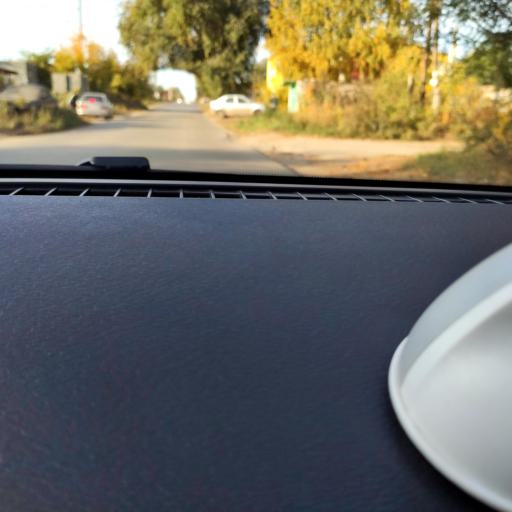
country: RU
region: Samara
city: Samara
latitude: 53.2356
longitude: 50.2407
